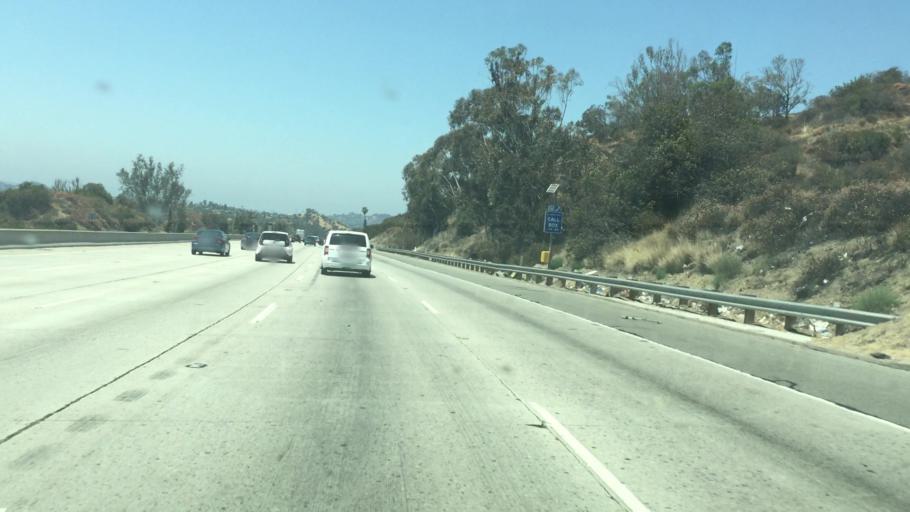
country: US
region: California
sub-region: Los Angeles County
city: La Canada Flintridge
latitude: 34.1478
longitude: -118.2012
